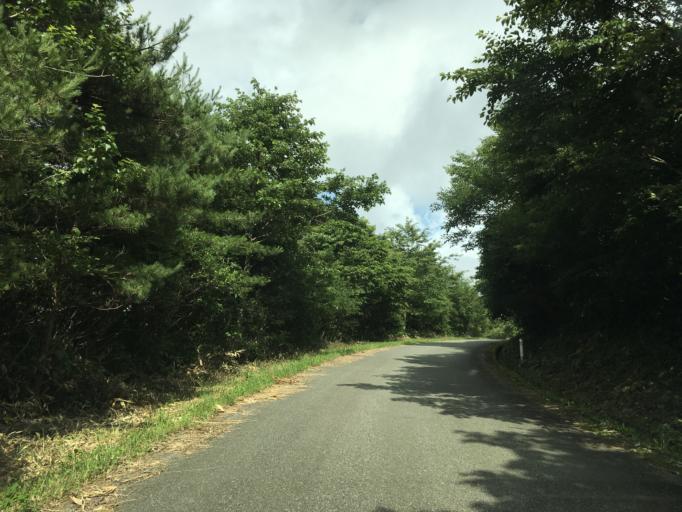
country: JP
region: Iwate
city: Ofunato
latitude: 38.9821
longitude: 141.4433
